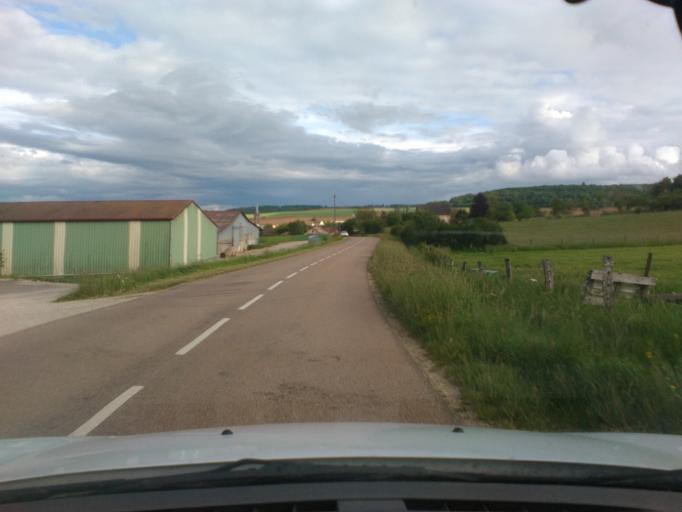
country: FR
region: Lorraine
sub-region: Departement des Vosges
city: Mirecourt
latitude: 48.3168
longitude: 6.0494
